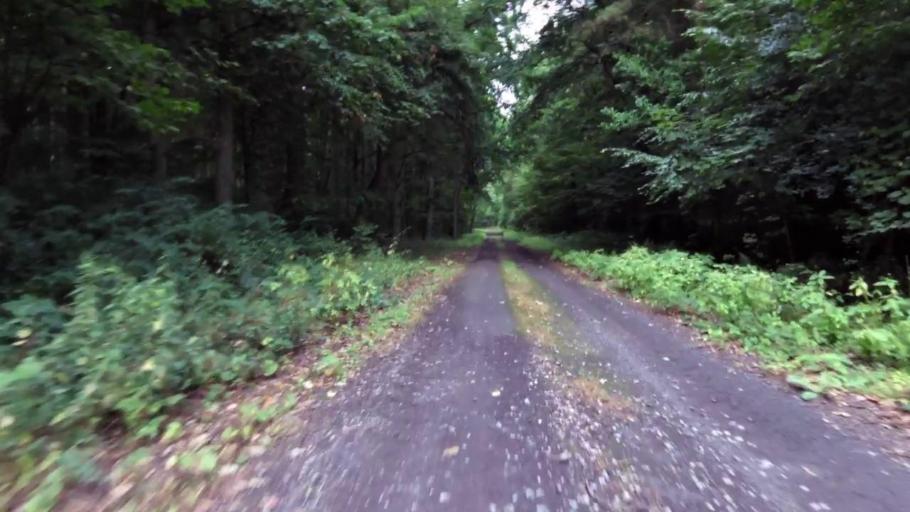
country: PL
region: West Pomeranian Voivodeship
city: Trzcinsko Zdroj
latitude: 52.8739
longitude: 14.6868
